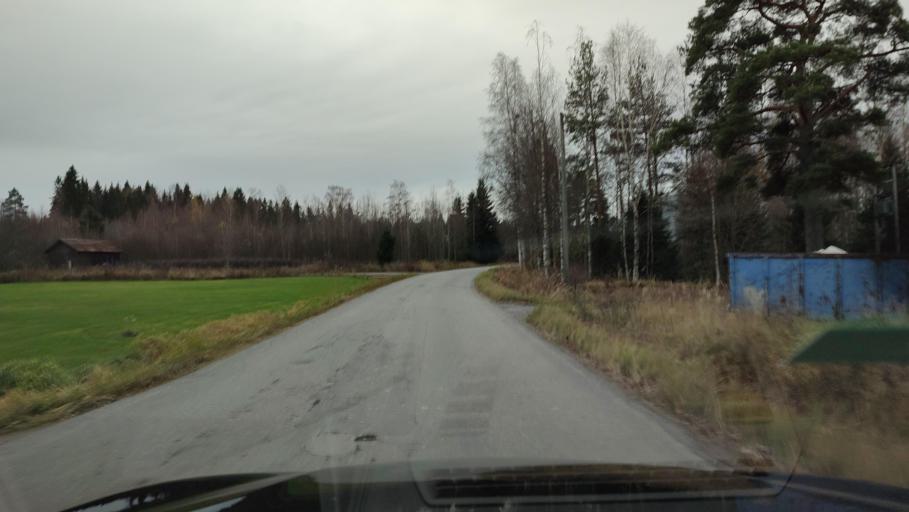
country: FI
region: Ostrobothnia
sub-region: Sydosterbotten
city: Naerpes
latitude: 62.4274
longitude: 21.4176
